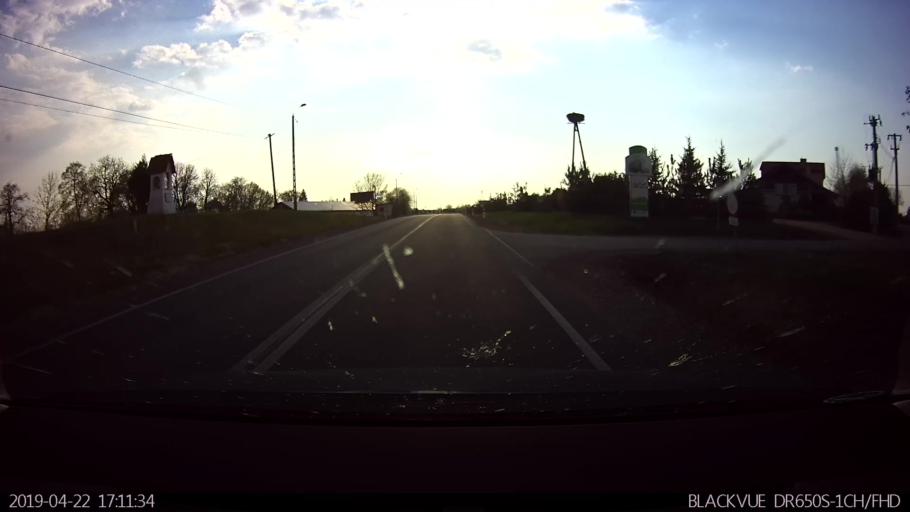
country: PL
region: Masovian Voivodeship
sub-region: Powiat siedlecki
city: Korczew
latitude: 52.4116
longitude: 22.5509
